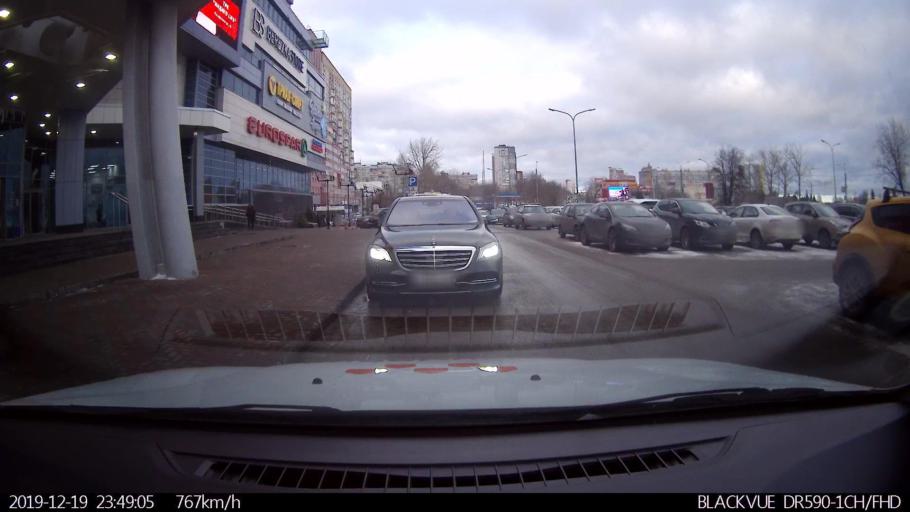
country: RU
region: Jaroslavl
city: Breytovo
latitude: 58.4464
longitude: 37.9340
